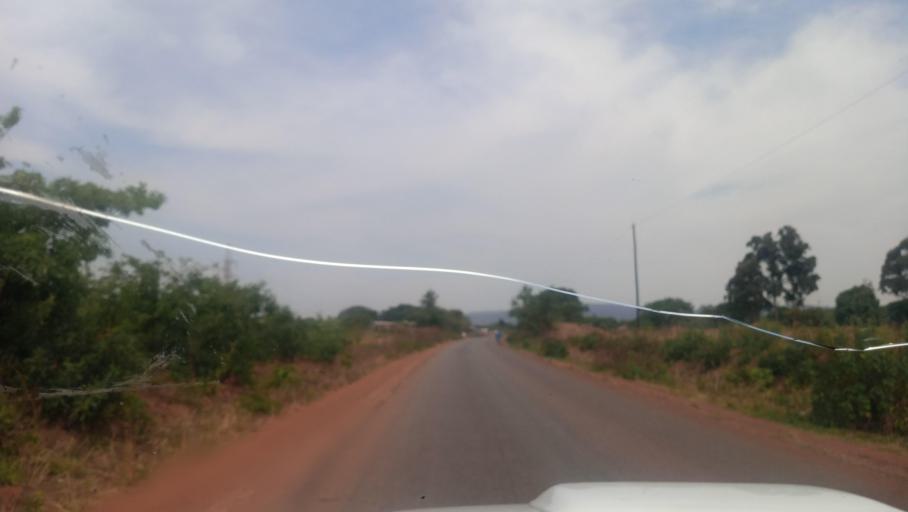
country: ZM
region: Northern
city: Mpika
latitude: -11.8329
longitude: 31.4200
